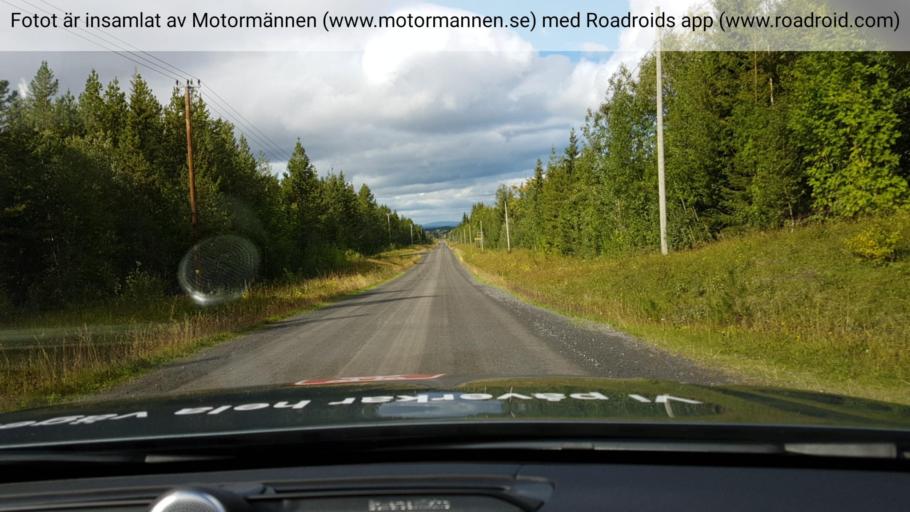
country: SE
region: Jaemtland
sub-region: OEstersunds Kommun
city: Lit
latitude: 63.6208
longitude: 14.9804
